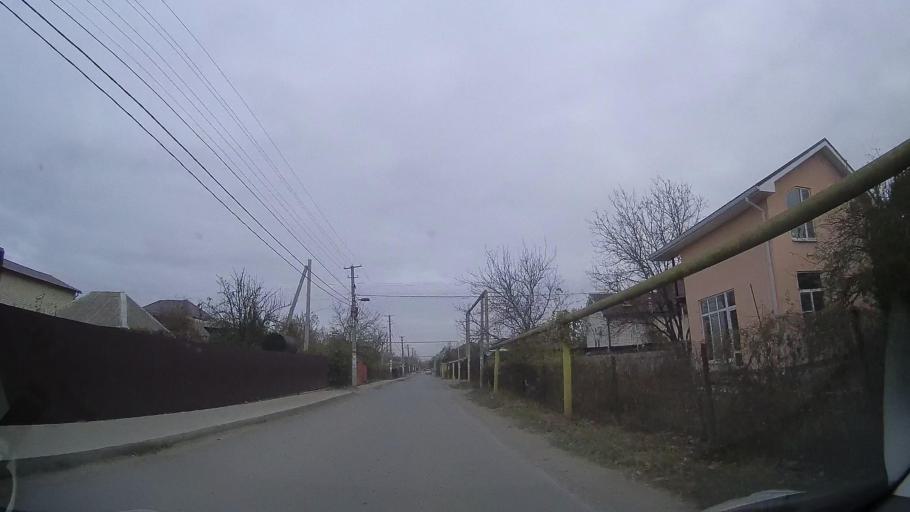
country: RU
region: Rostov
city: Bataysk
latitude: 47.0831
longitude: 39.7616
